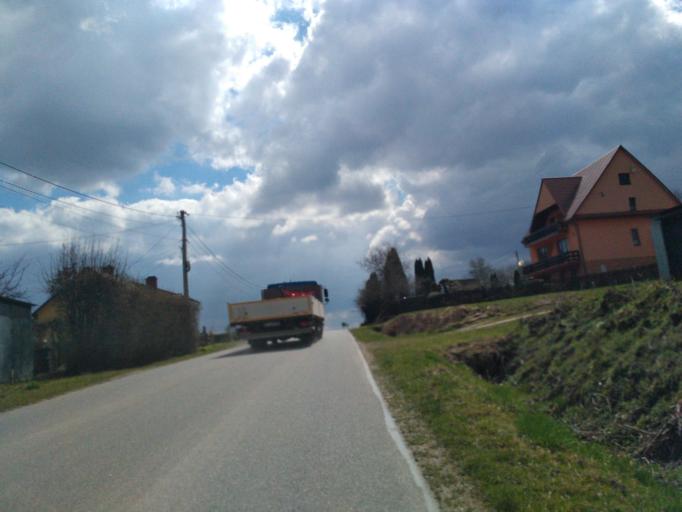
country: PL
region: Subcarpathian Voivodeship
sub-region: Powiat brzozowski
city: Dydnia
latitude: 49.6554
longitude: 22.2025
